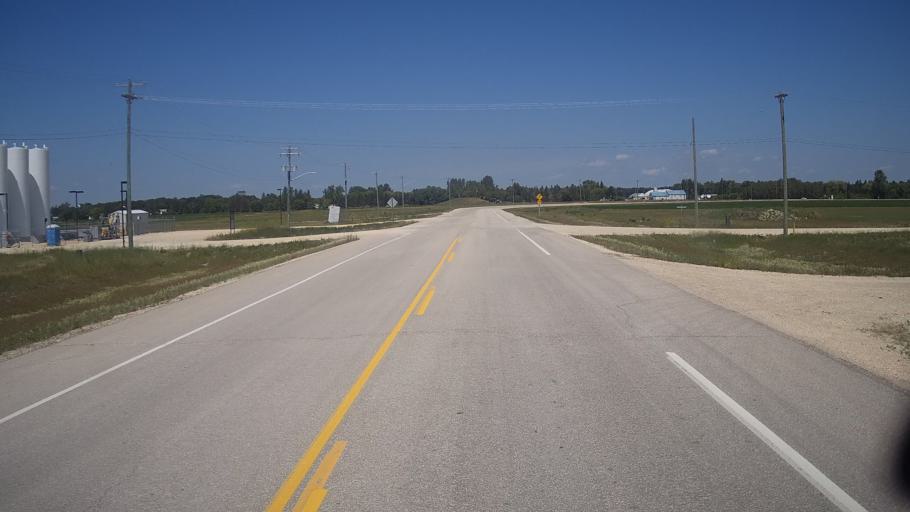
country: CA
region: Manitoba
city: Stonewall
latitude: 50.1236
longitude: -97.5443
